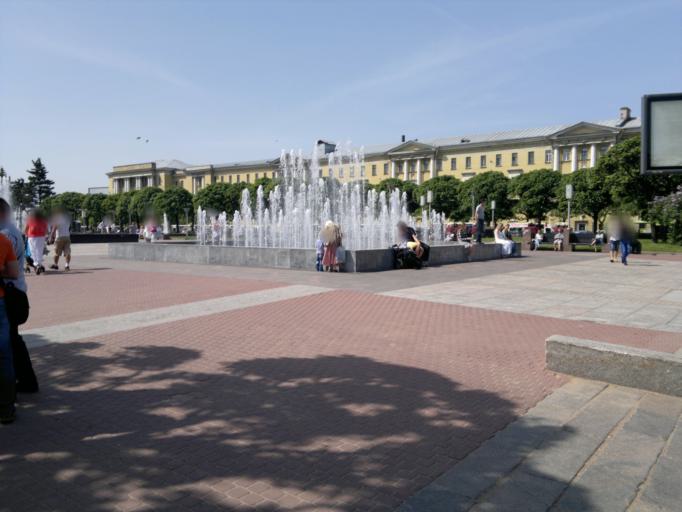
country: RU
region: Leningrad
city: Finlyandskiy
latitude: 59.9549
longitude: 30.3563
